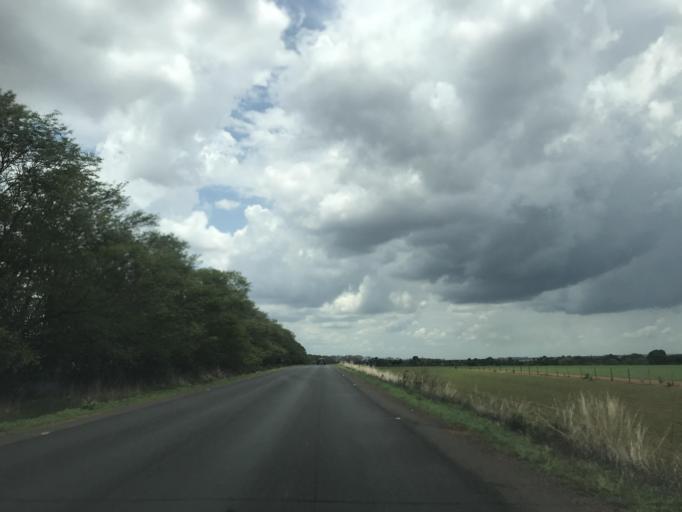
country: BR
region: Goias
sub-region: Vianopolis
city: Vianopolis
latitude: -16.8001
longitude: -48.5197
